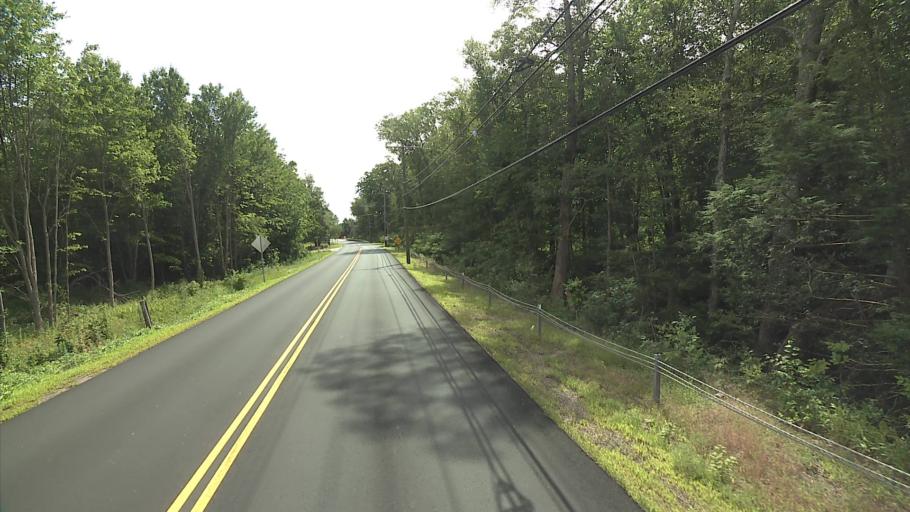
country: US
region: Connecticut
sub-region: Windham County
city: South Woodstock
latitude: 41.9376
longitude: -71.9859
